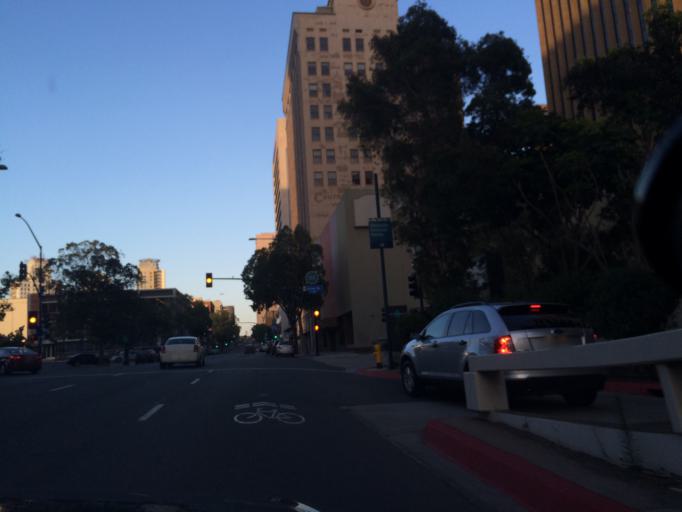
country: US
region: California
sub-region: San Diego County
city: San Diego
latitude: 32.7188
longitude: -117.1634
